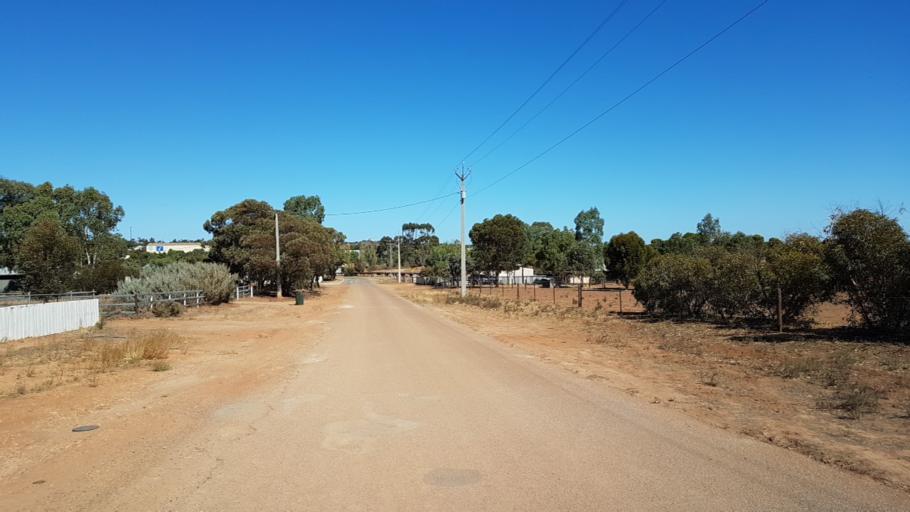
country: AU
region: South Australia
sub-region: Peterborough
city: Peterborough
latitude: -32.9698
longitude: 138.8256
